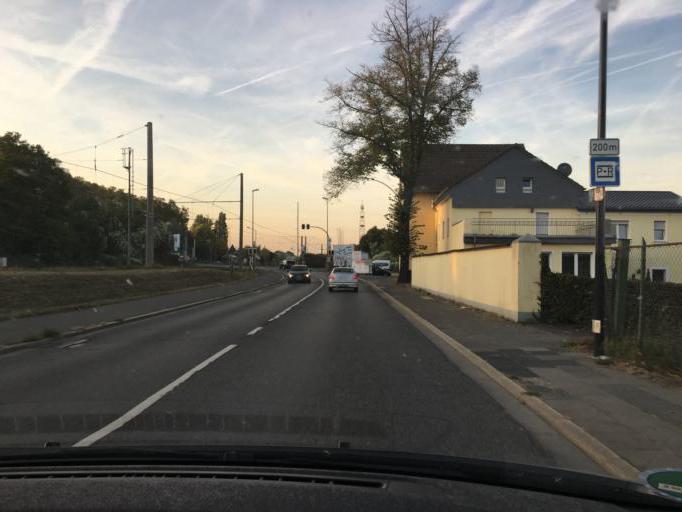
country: DE
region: North Rhine-Westphalia
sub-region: Regierungsbezirk Koln
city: Hurth
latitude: 50.8626
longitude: 6.8992
